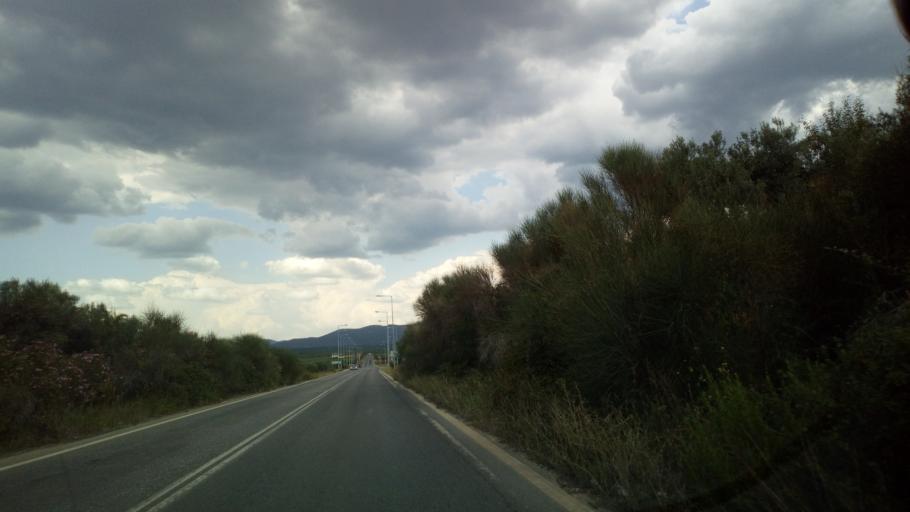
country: GR
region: Central Macedonia
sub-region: Nomos Chalkidikis
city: Kalyves Polygyrou
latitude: 40.2815
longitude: 23.4304
